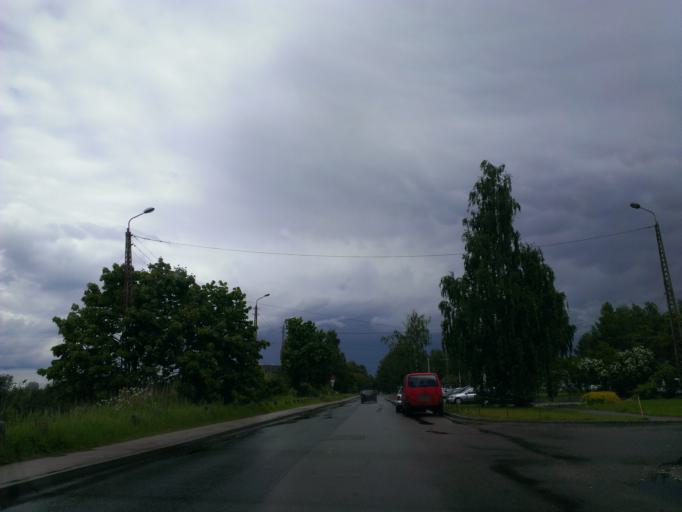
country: LV
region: Riga
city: Riga
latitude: 56.9321
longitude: 24.0929
